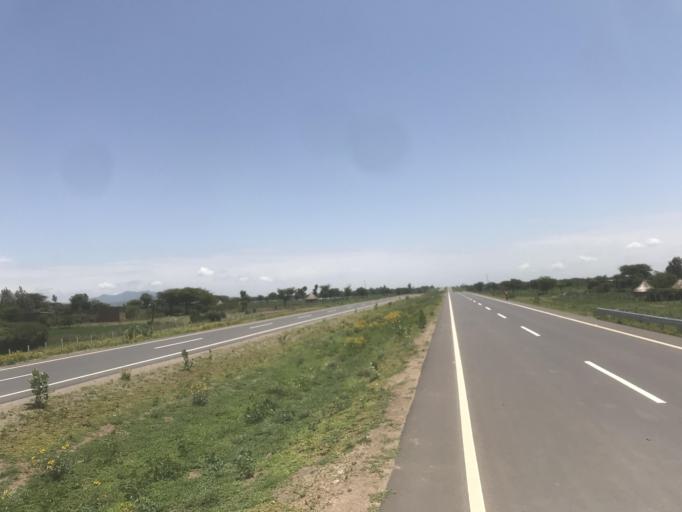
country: ET
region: Oromiya
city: Mojo
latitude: 8.3777
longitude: 39.0013
